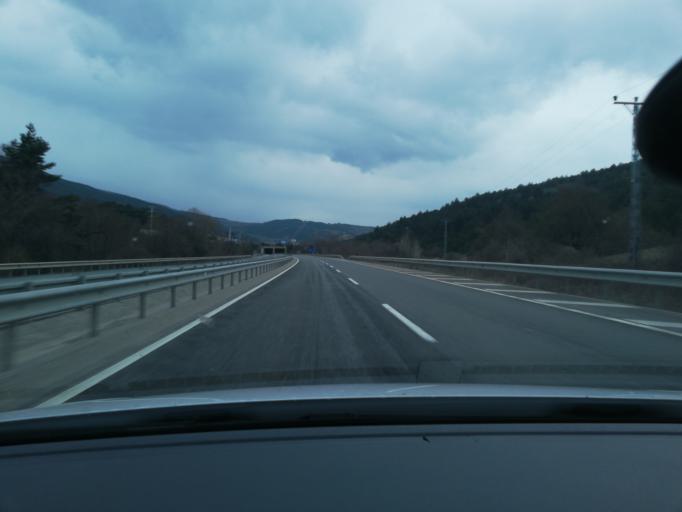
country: TR
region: Bolu
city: Gokcesu
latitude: 40.7412
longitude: 31.8342
